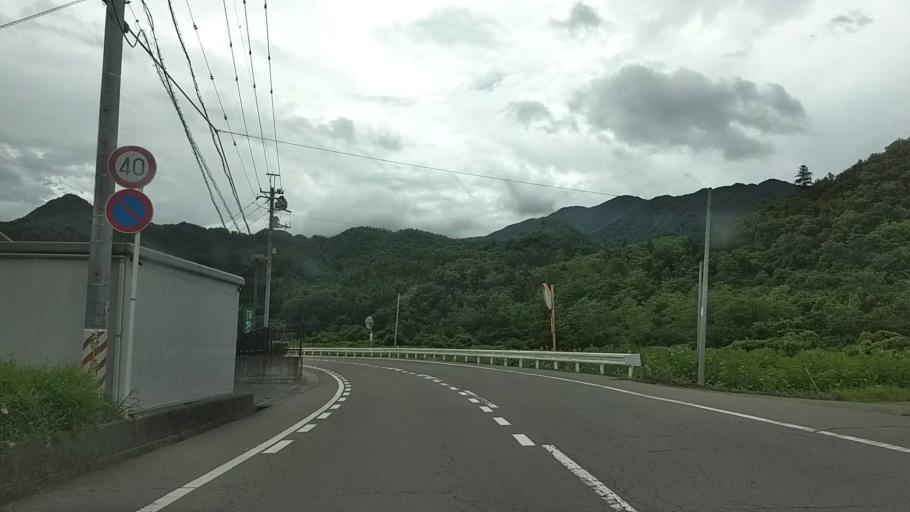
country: JP
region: Yamanashi
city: Otsuki
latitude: 35.5593
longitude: 138.9488
